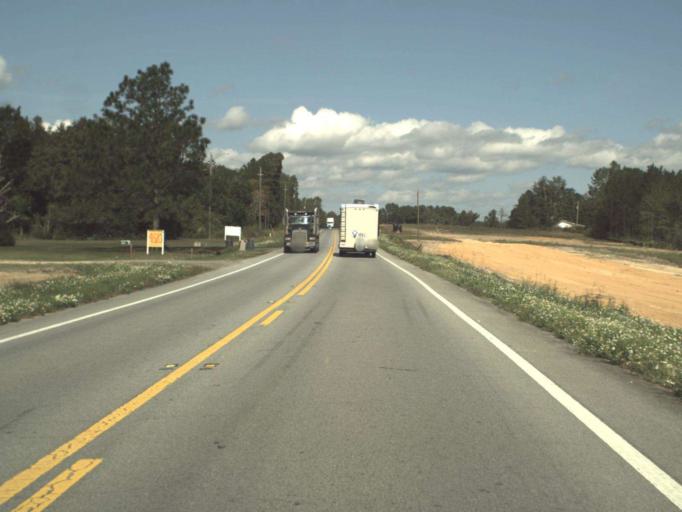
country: US
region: Florida
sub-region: Walton County
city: DeFuniak Springs
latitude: 30.6532
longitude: -86.1154
